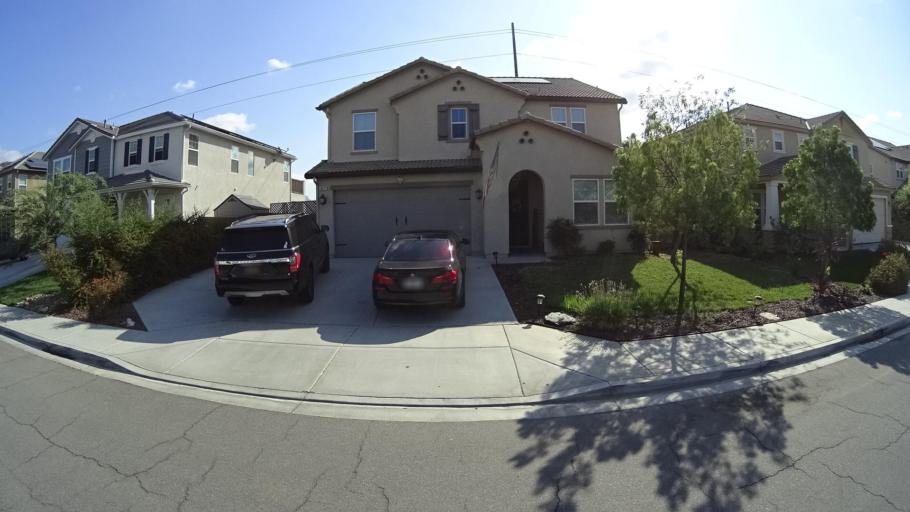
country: US
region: California
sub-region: San Diego County
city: Eucalyptus Hills
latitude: 32.8591
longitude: -116.9576
